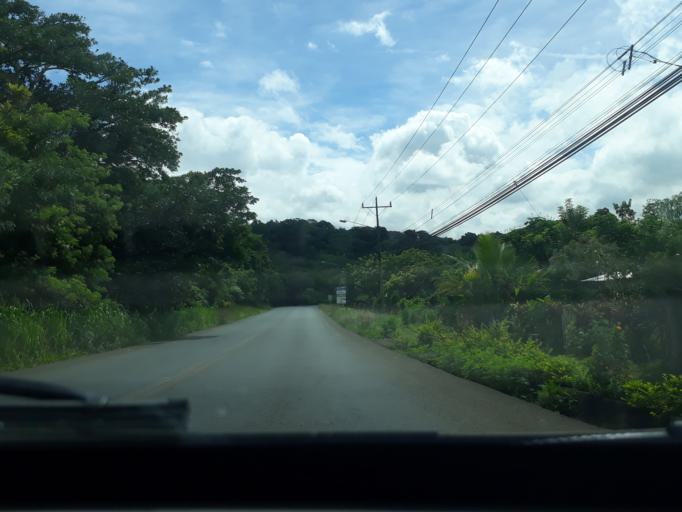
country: CR
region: Alajuela
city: Atenas
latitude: 10.0366
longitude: -84.3509
